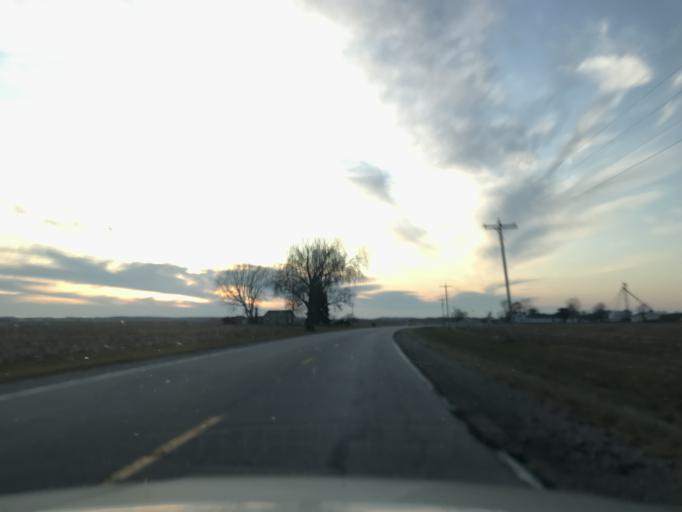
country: US
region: Illinois
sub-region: Henderson County
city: Oquawka
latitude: 41.0186
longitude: -90.7936
